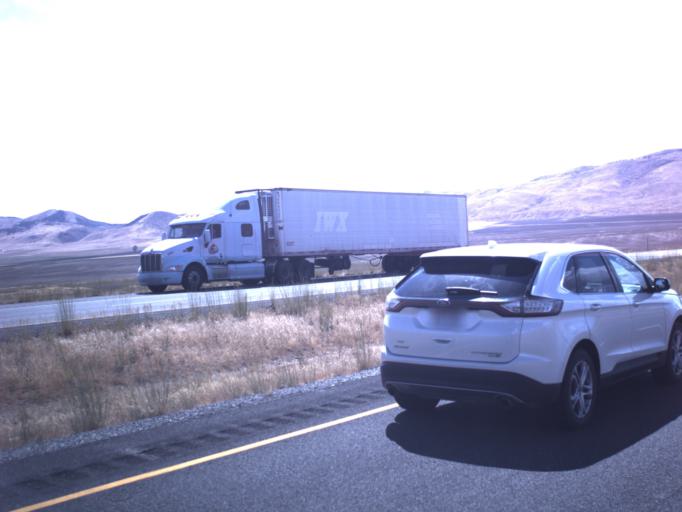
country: US
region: Idaho
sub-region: Oneida County
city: Malad City
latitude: 41.9077
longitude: -112.5912
